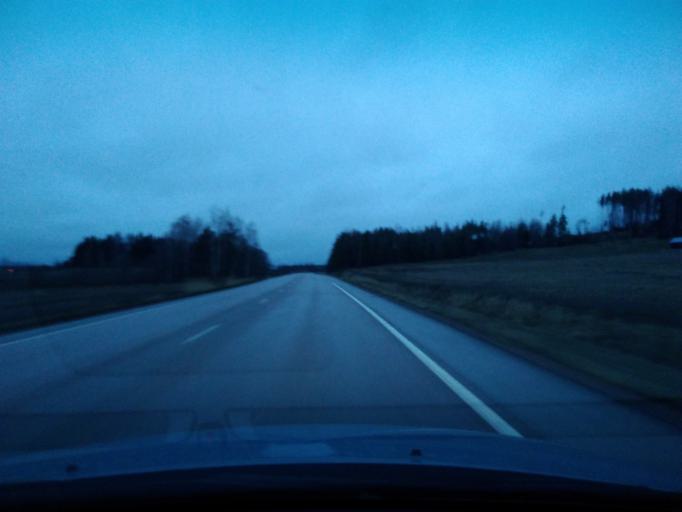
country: FI
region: Uusimaa
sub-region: Porvoo
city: Askola
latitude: 60.4653
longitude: 25.5752
